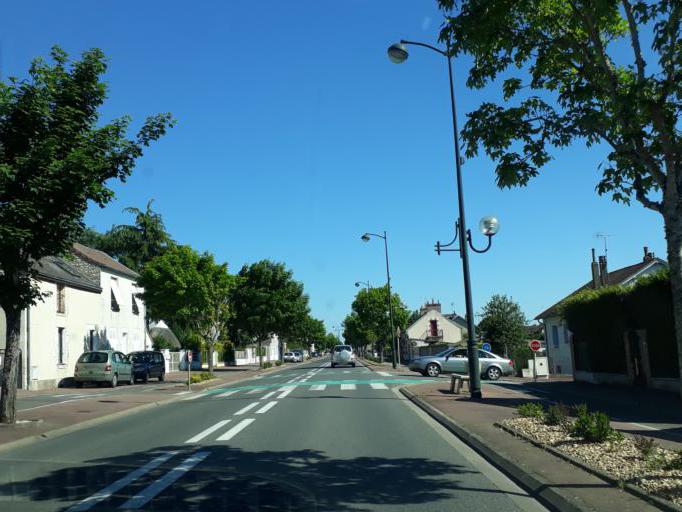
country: FR
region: Centre
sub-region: Departement du Loiret
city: Briare
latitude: 47.6509
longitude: 2.7258
